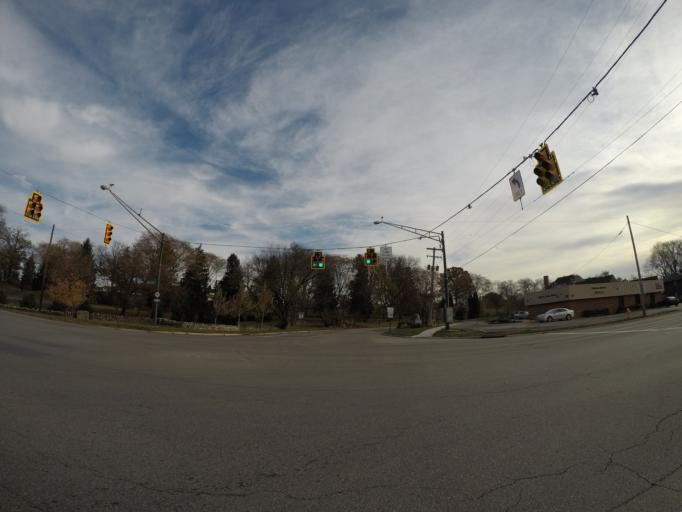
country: US
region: Ohio
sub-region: Franklin County
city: Upper Arlington
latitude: 39.9990
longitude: -83.0760
